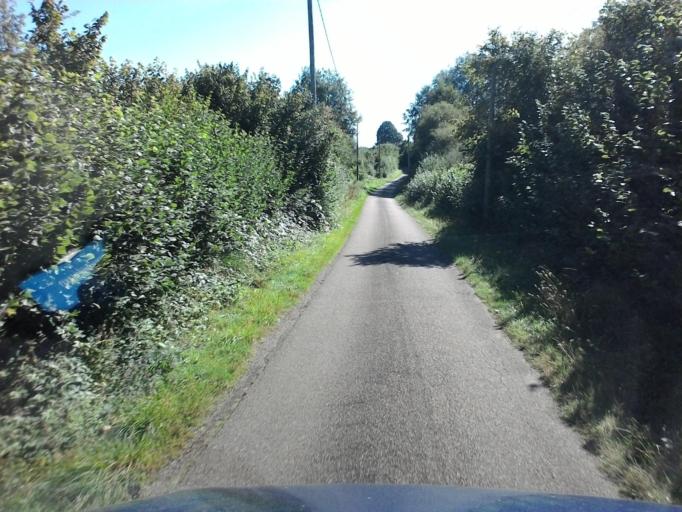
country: FR
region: Bourgogne
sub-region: Departement de la Cote-d'Or
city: Saulieu
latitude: 47.2512
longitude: 4.2161
